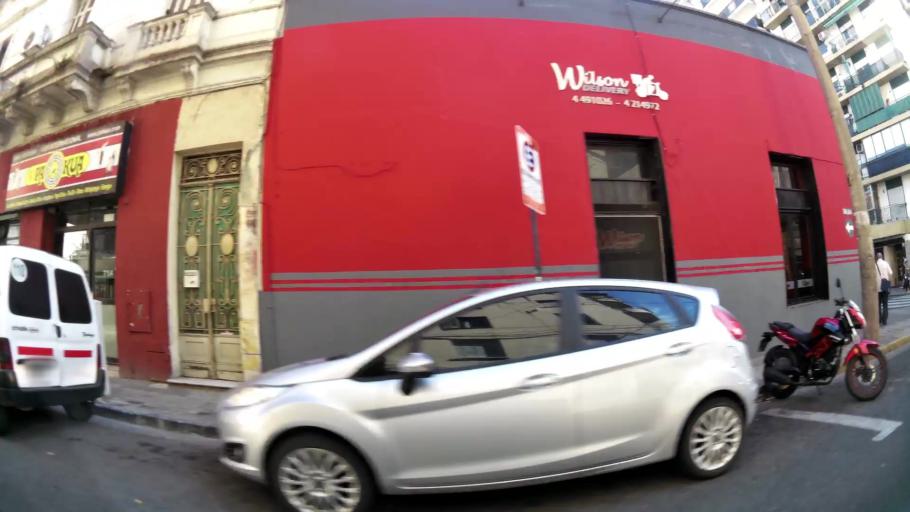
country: AR
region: Santa Fe
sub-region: Departamento de Rosario
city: Rosario
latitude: -32.9513
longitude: -60.6337
